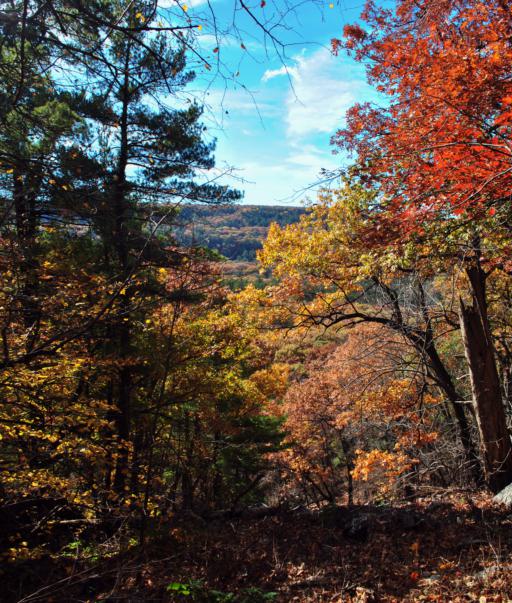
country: US
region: Wisconsin
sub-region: Sauk County
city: Baraboo
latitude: 43.4134
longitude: -89.7184
